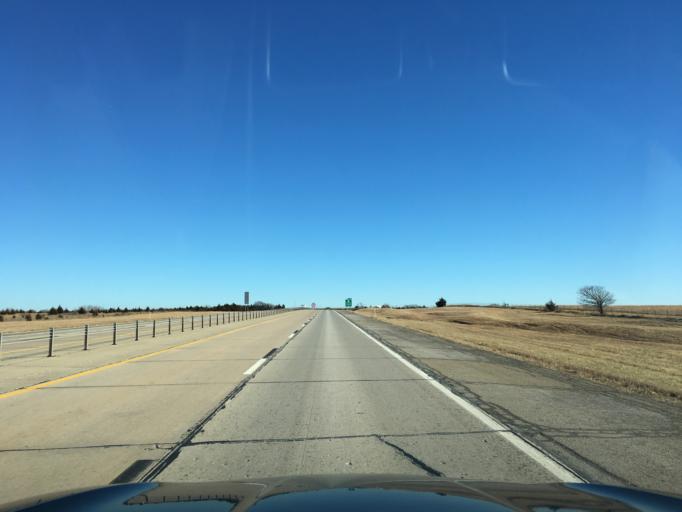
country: US
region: Oklahoma
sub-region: Pawnee County
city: Pawnee
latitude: 36.2247
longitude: -96.8101
